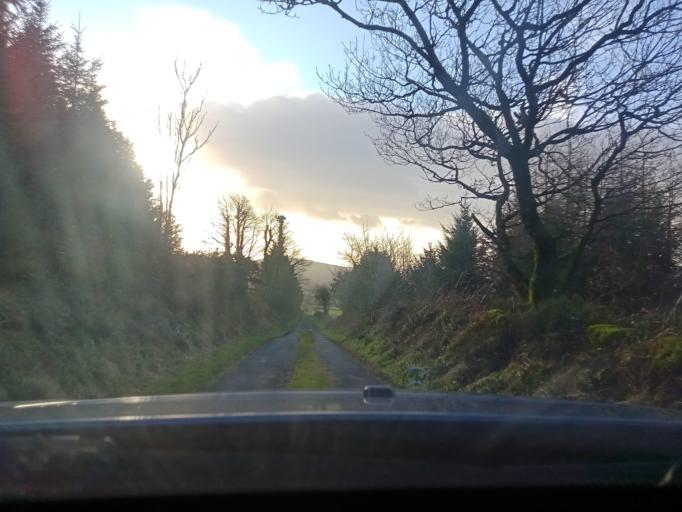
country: IE
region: Leinster
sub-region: Kilkenny
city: Callan
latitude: 52.4648
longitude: -7.4220
